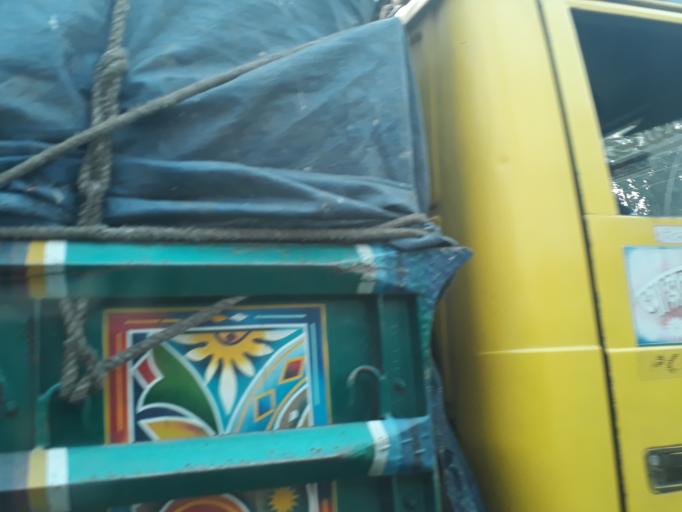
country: BD
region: Khulna
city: Bhatpara Abhaynagar
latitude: 22.9676
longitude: 89.4773
